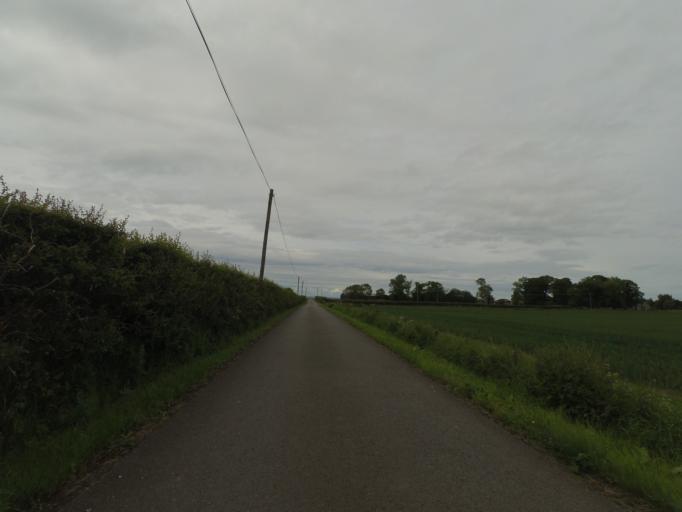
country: GB
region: Scotland
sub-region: East Lothian
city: Macmerry
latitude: 55.9437
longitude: -2.9169
